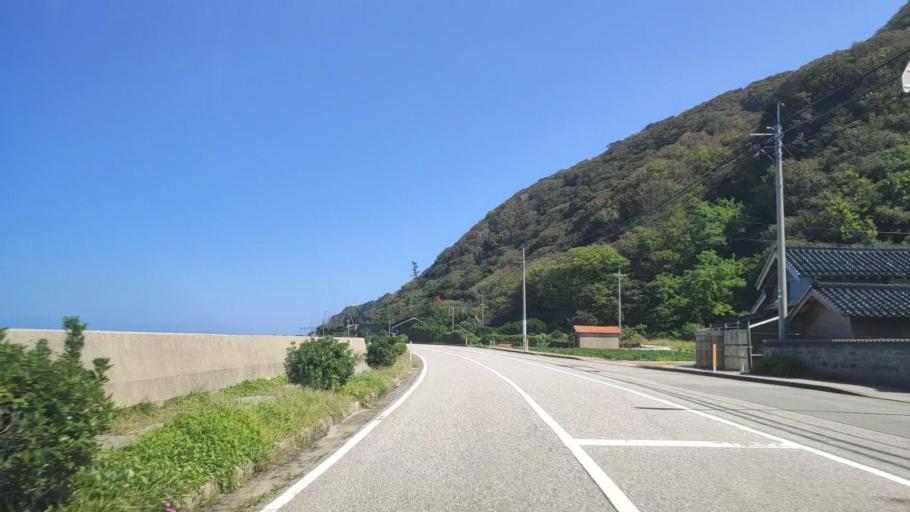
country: JP
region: Ishikawa
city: Nanao
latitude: 37.4935
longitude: 137.1315
